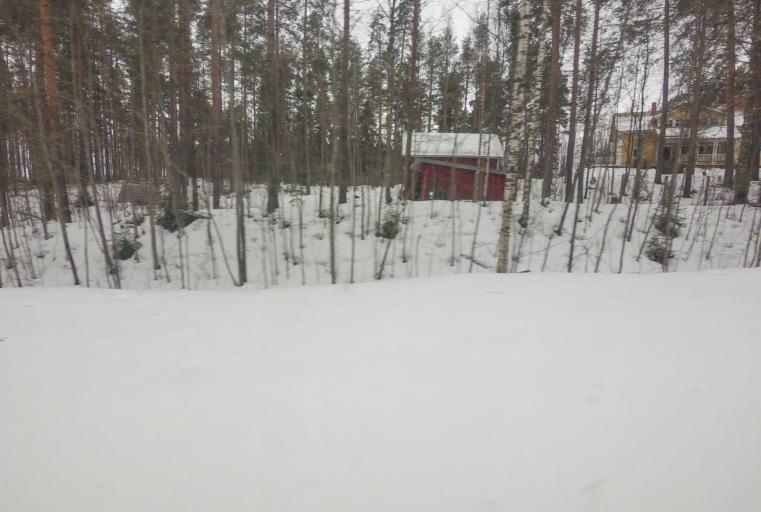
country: FI
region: Southern Savonia
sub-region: Savonlinna
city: Savonlinna
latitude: 61.8643
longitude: 28.9109
